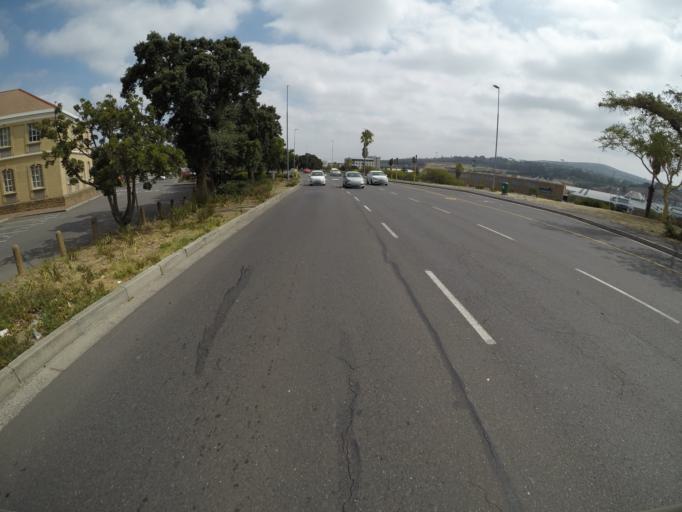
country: ZA
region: Western Cape
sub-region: City of Cape Town
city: Kraaifontein
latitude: -33.8749
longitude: 18.6372
